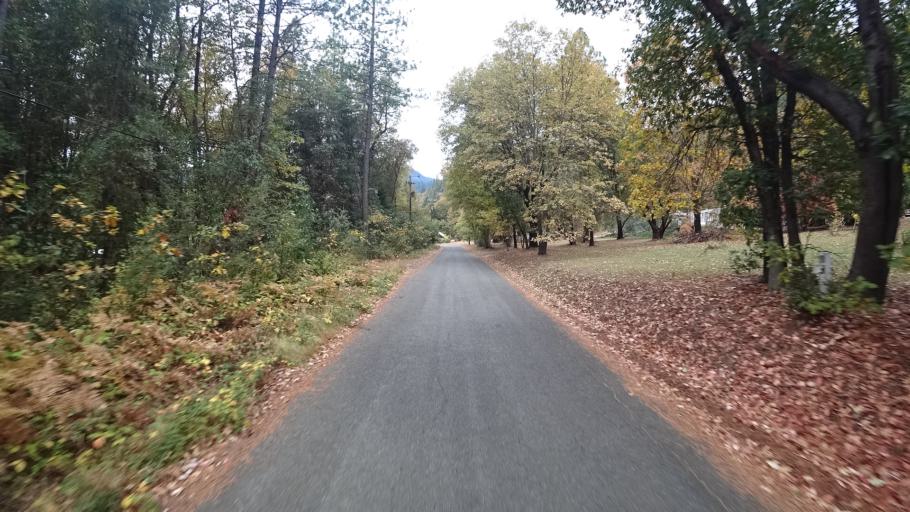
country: US
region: California
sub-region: Siskiyou County
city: Happy Camp
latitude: 41.8480
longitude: -123.1943
